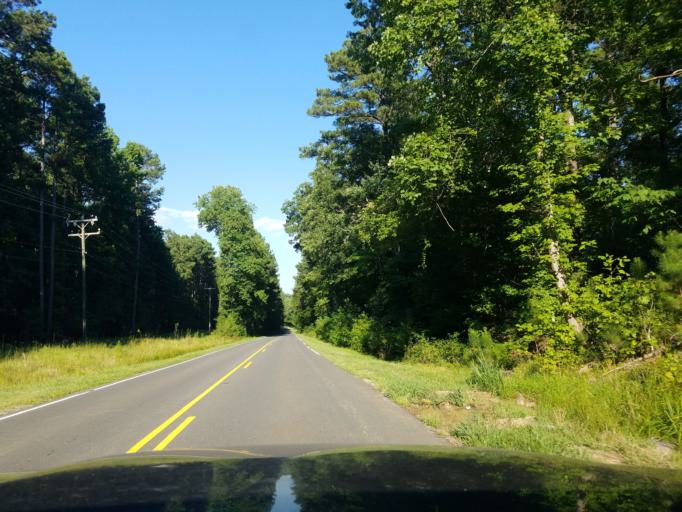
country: US
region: North Carolina
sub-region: Wake County
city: Green Level
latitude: 35.8762
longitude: -78.9478
